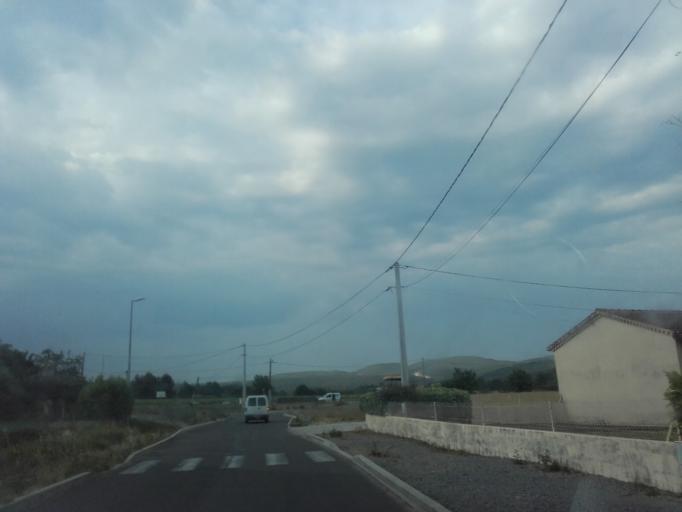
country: FR
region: Rhone-Alpes
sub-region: Departement de l'Ardeche
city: Ruoms
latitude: 44.4175
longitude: 4.4116
